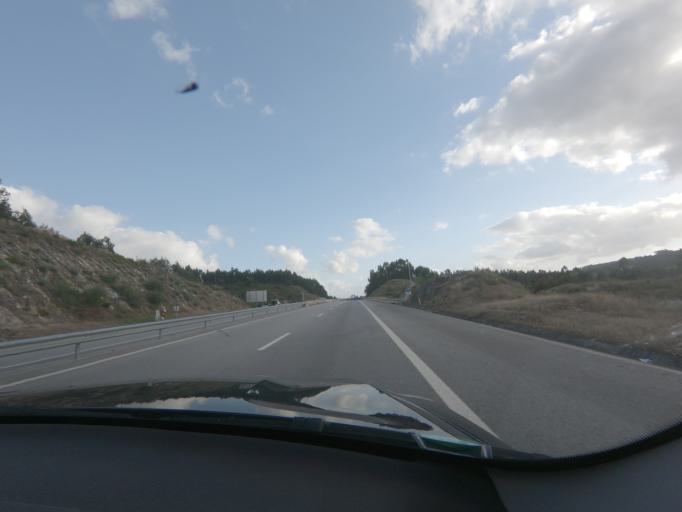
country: PT
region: Viseu
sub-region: Viseu
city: Viseu
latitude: 40.6331
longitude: -7.9588
